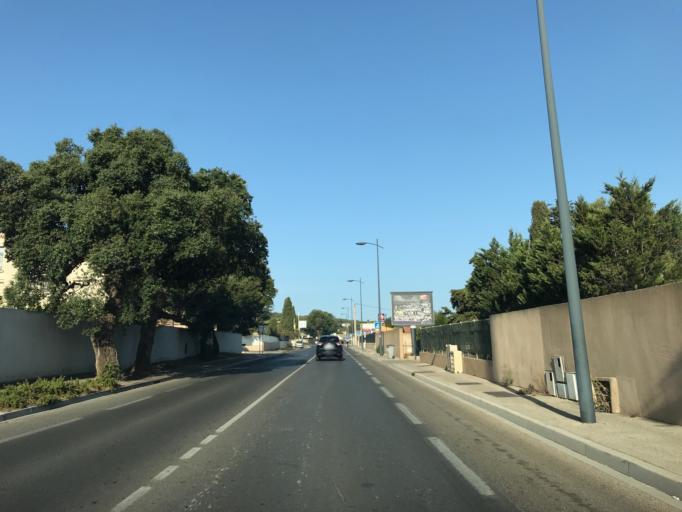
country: FR
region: Provence-Alpes-Cote d'Azur
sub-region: Departement du Var
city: Six-Fours-les-Plages
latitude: 43.0842
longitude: 5.8641
